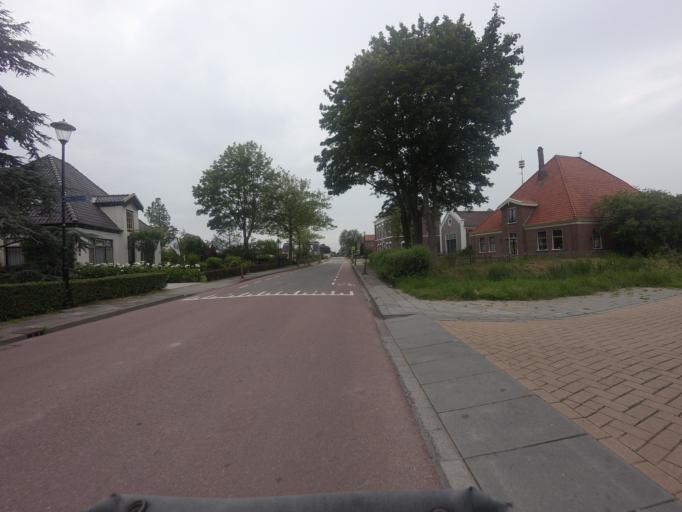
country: NL
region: North Holland
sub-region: Gemeente Hoorn
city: Hoorn
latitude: 52.6850
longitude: 5.1341
